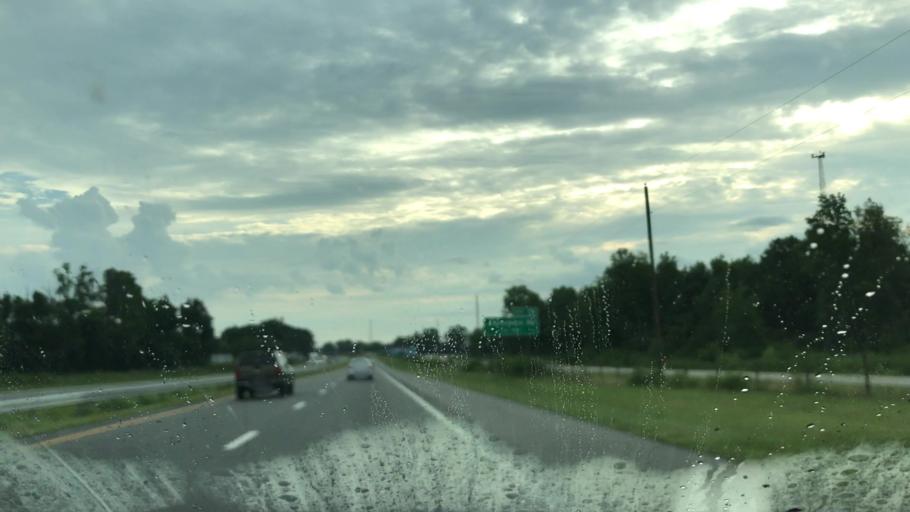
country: US
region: North Carolina
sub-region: Harnett County
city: Dunn
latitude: 35.3102
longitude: -78.5833
